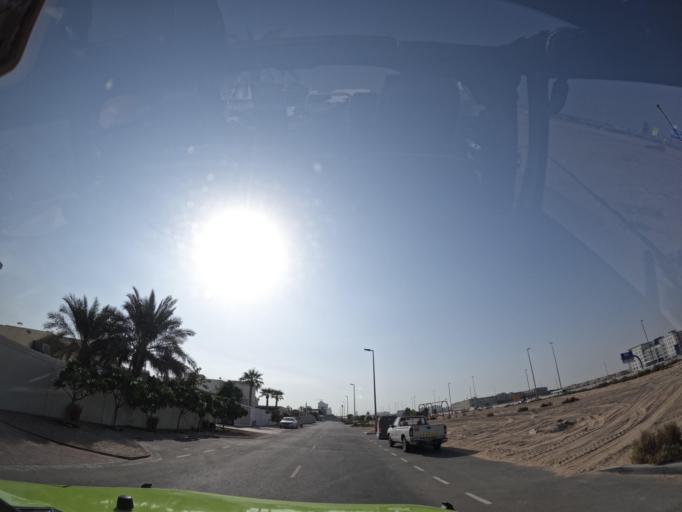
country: AE
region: Dubai
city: Dubai
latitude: 25.1308
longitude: 55.3571
